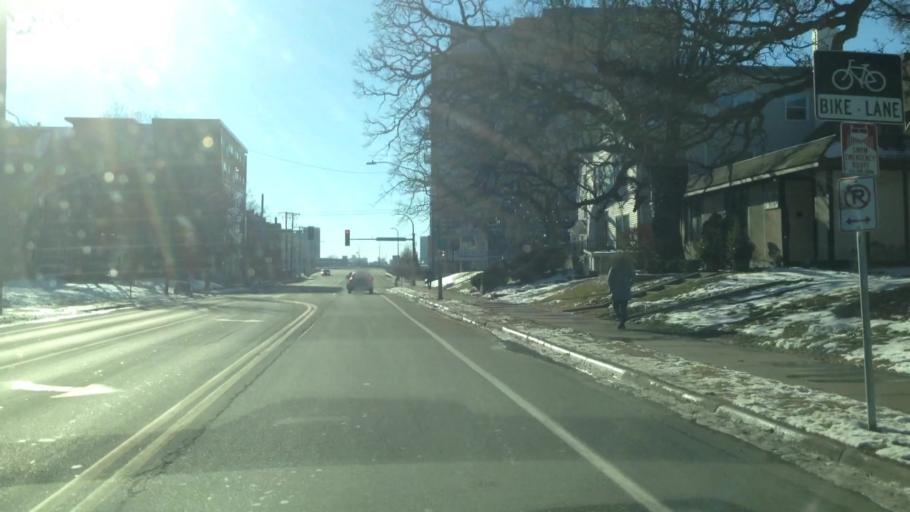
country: US
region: Minnesota
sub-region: Hennepin County
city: Minneapolis
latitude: 44.9826
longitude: -93.2415
